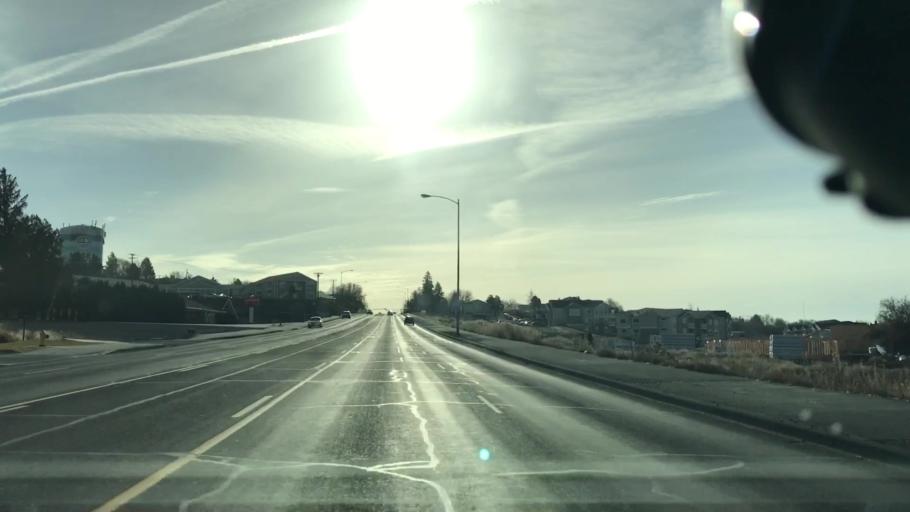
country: US
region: Washington
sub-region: Grant County
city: Moses Lake
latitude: 47.1276
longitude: -119.2692
